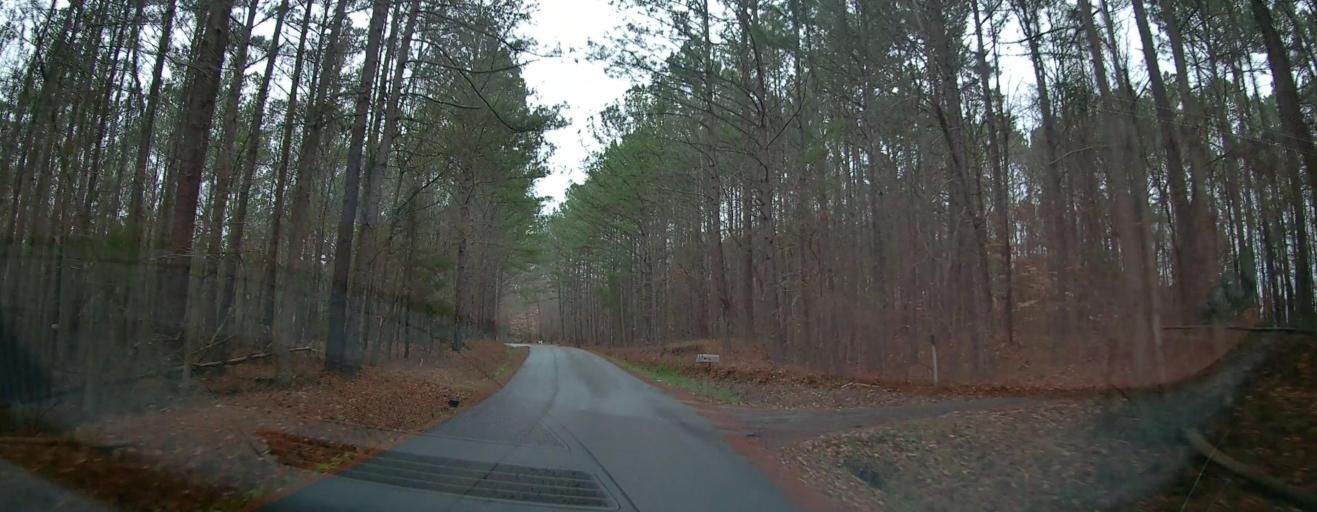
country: US
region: Georgia
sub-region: Monroe County
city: Forsyth
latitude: 33.0490
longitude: -83.8836
